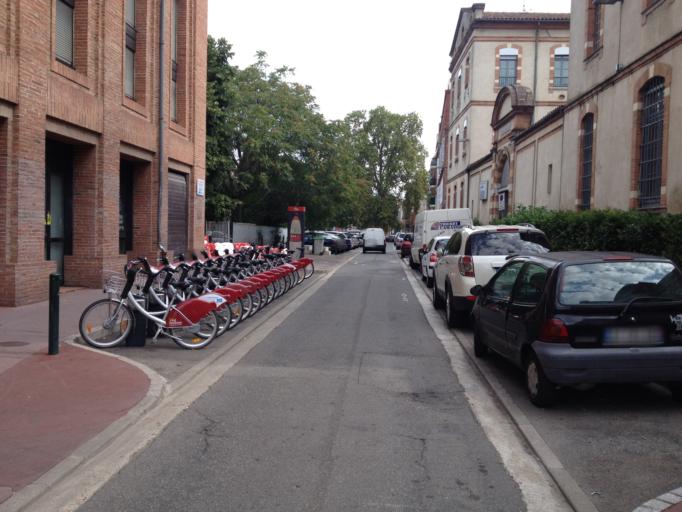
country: FR
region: Midi-Pyrenees
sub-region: Departement de la Haute-Garonne
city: Toulouse
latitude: 43.6050
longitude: 1.4372
